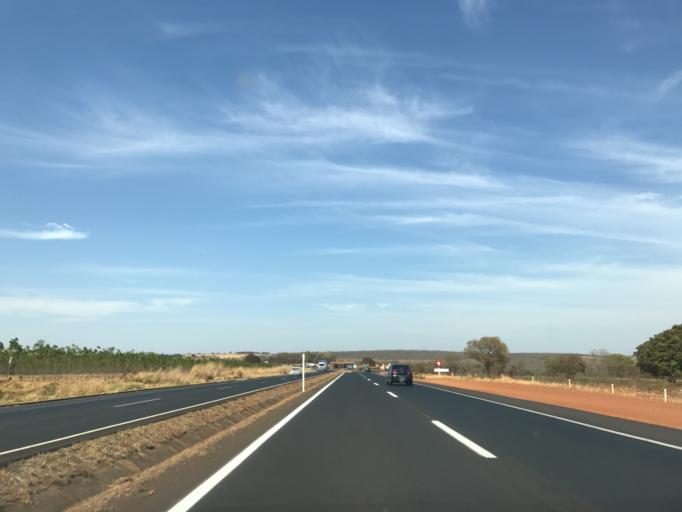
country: BR
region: Minas Gerais
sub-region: Monte Alegre De Minas
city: Monte Alegre de Minas
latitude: -18.8108
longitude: -49.0855
